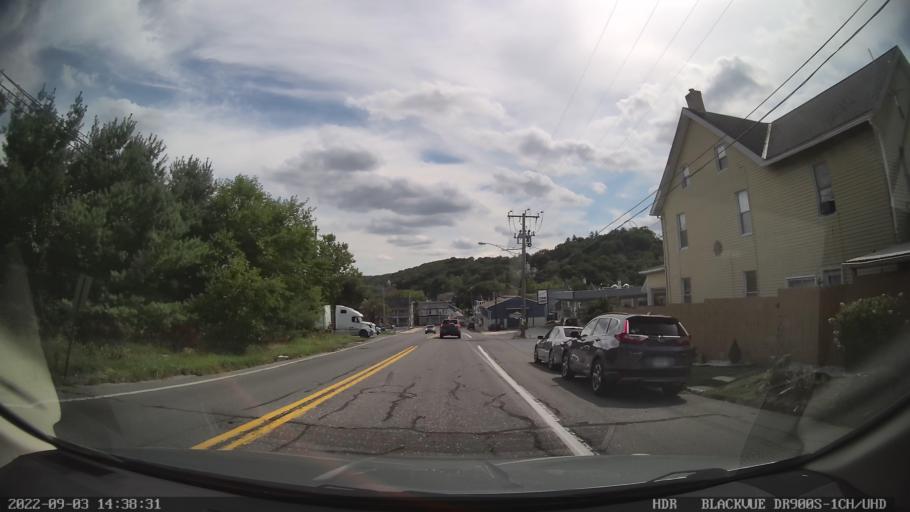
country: US
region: Pennsylvania
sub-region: Northampton County
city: Walnutport
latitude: 40.7548
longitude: -75.6055
